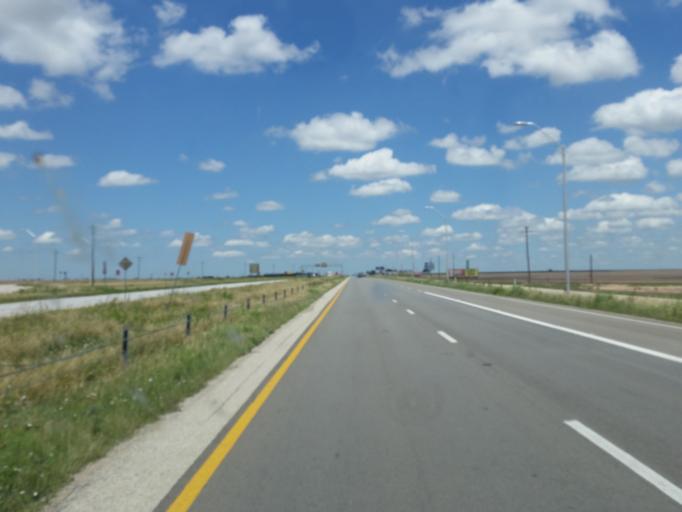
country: US
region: Texas
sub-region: Nolan County
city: Roscoe
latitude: 32.4475
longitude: -100.4989
